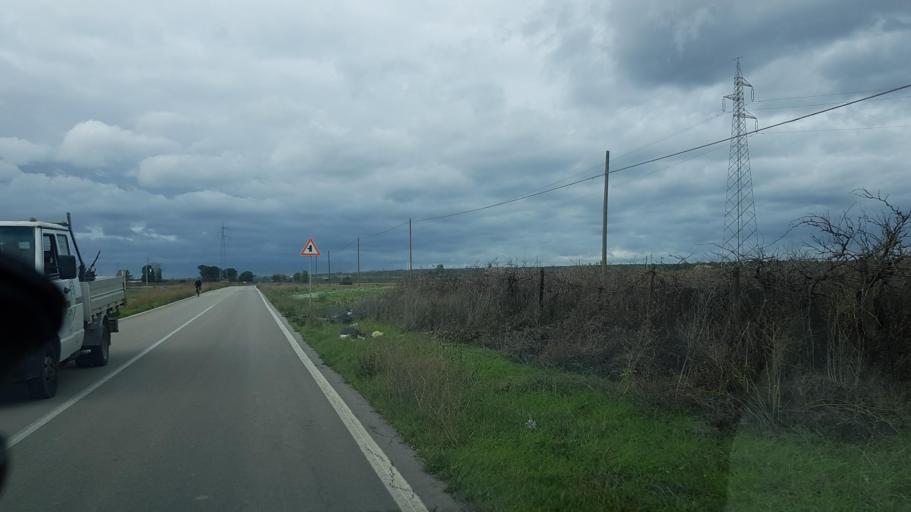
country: IT
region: Apulia
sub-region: Provincia di Brindisi
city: Francavilla Fontana
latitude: 40.5421
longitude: 17.5626
